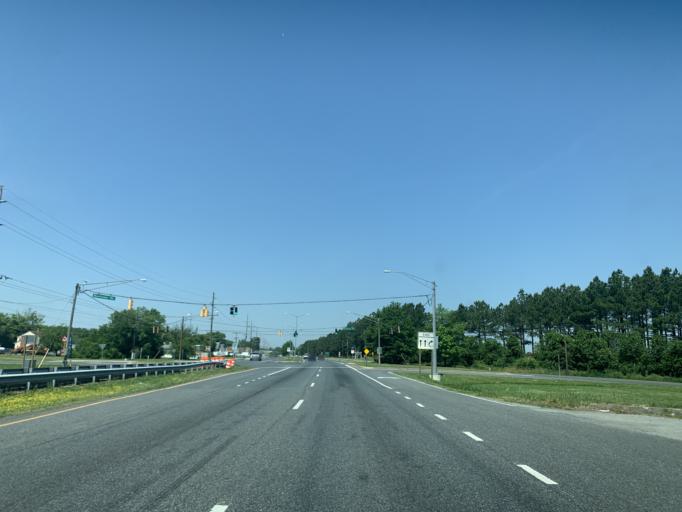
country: US
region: Maryland
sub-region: Dorchester County
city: Cambridge
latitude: 38.5535
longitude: -76.0421
